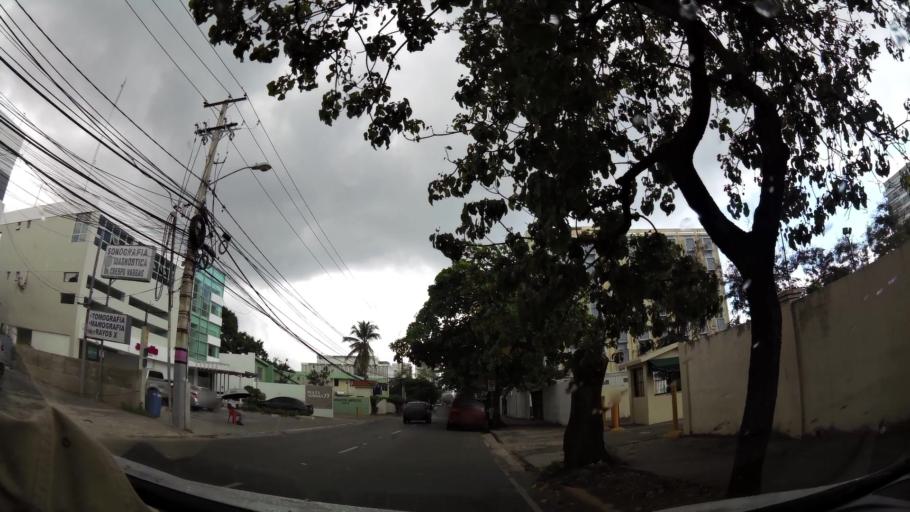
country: DO
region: Nacional
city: Ciudad Nueva
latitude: 18.4716
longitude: -69.9137
